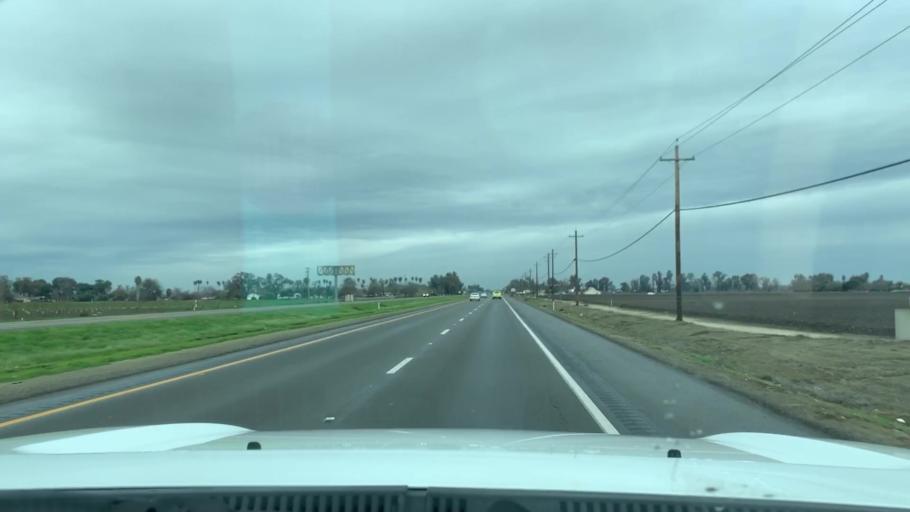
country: US
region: California
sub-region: Kings County
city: Lemoore
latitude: 36.3231
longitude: -119.8078
